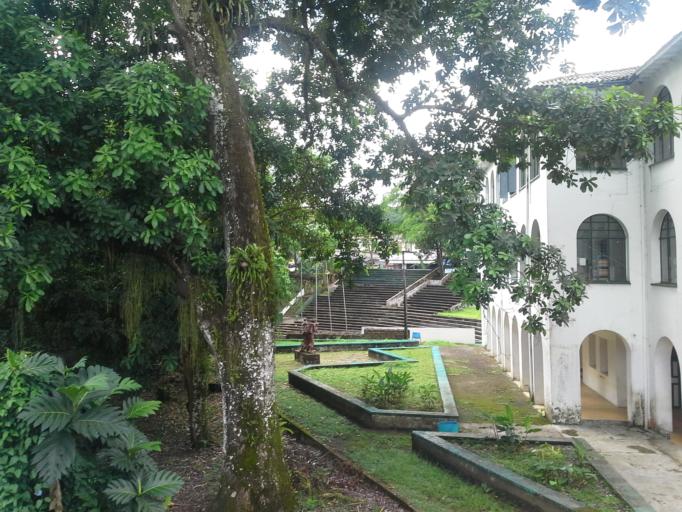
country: CO
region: Caqueta
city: Florencia
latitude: 1.6133
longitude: -75.6123
